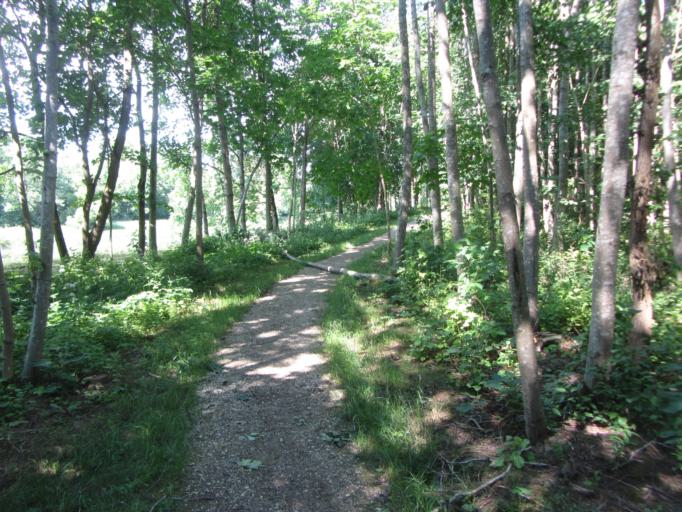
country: LT
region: Panevezys
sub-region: Birzai
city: Birzai
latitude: 56.3852
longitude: 24.7013
